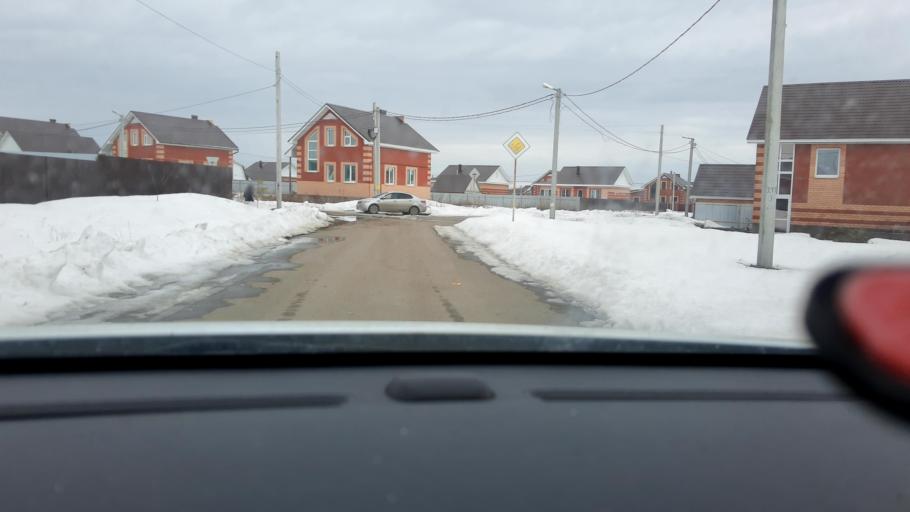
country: RU
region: Bashkortostan
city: Kabakovo
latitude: 54.6119
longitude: 56.1239
